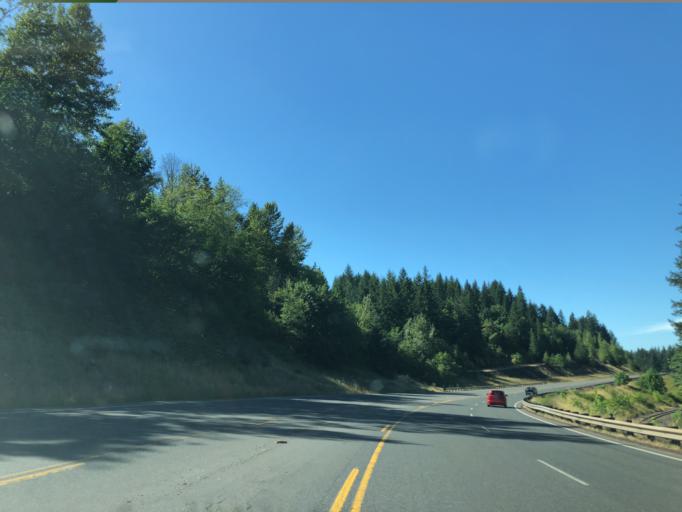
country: US
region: Oregon
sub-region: Linn County
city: Sweet Home
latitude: 44.4061
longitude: -122.7624
